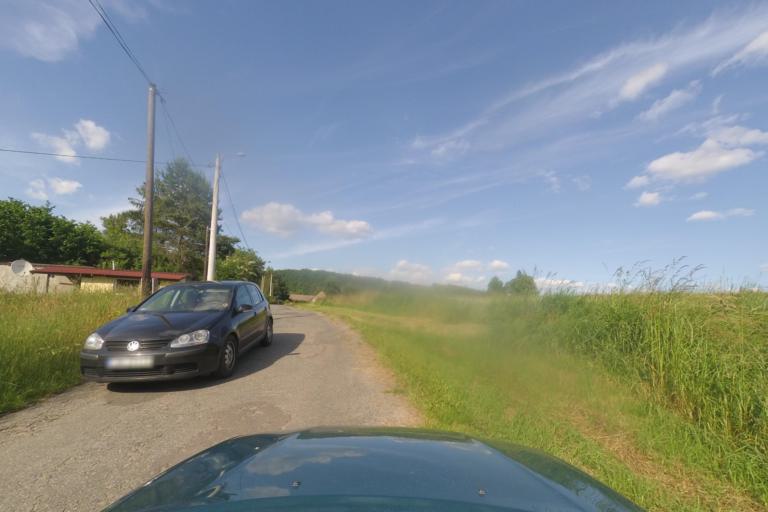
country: PL
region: Lower Silesian Voivodeship
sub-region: Powiat zabkowicki
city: Bardo
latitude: 50.4971
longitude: 16.6871
